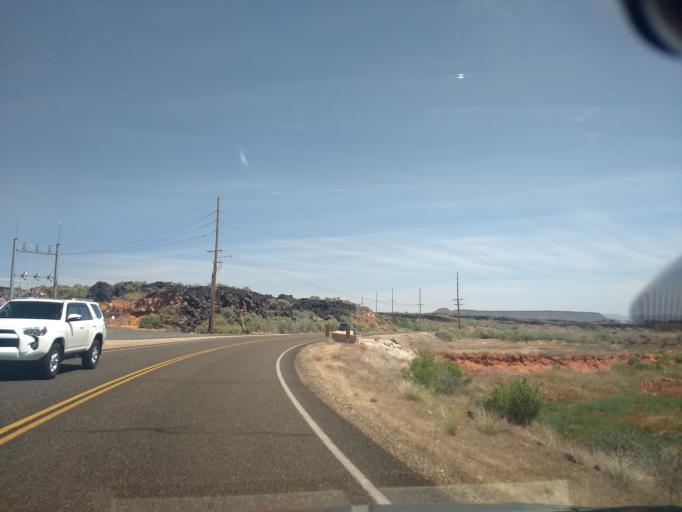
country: US
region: Utah
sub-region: Washington County
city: Santa Clara
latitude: 37.1468
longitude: -113.6545
